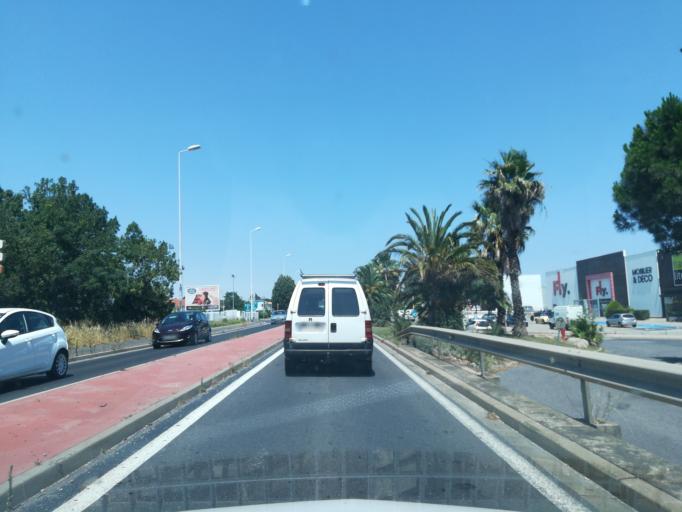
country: FR
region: Languedoc-Roussillon
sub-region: Departement des Pyrenees-Orientales
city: Perpignan
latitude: 42.6759
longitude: 2.8896
